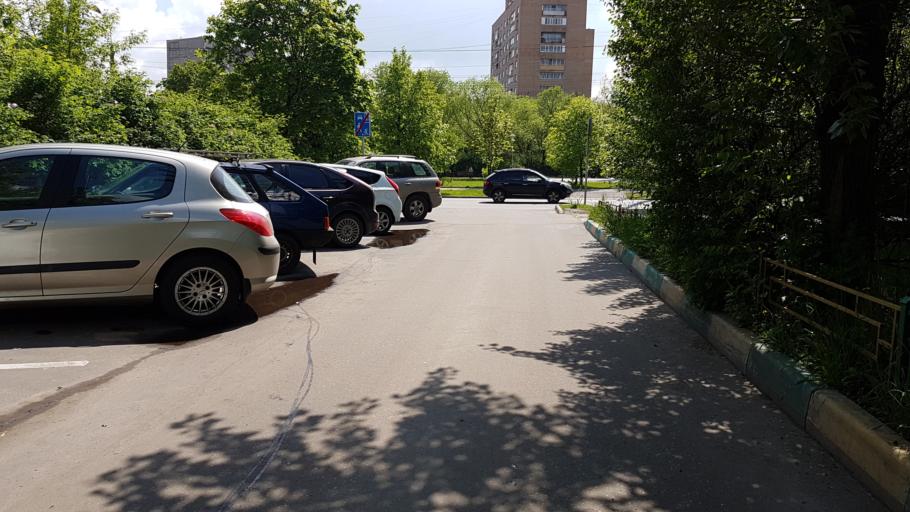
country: RU
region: Moskovskaya
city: Novogireyevo
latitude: 55.7505
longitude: 37.8266
